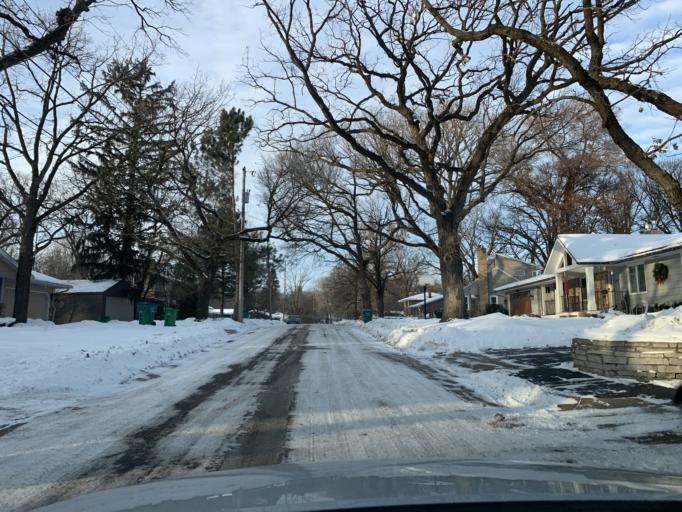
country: US
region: Minnesota
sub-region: Hennepin County
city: Minnetonka Mills
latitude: 44.9456
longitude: -93.3971
